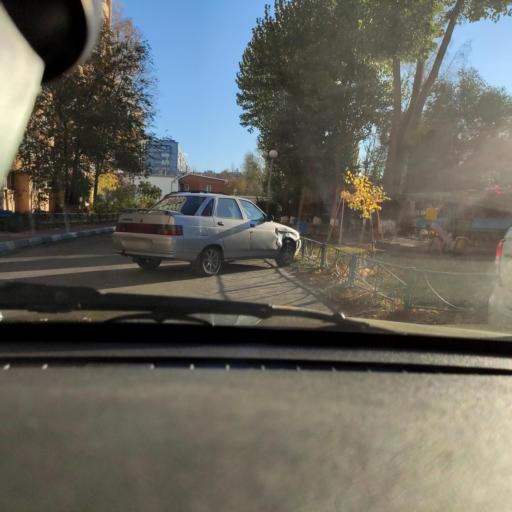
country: RU
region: Samara
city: Tol'yatti
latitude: 53.5114
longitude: 49.2704
